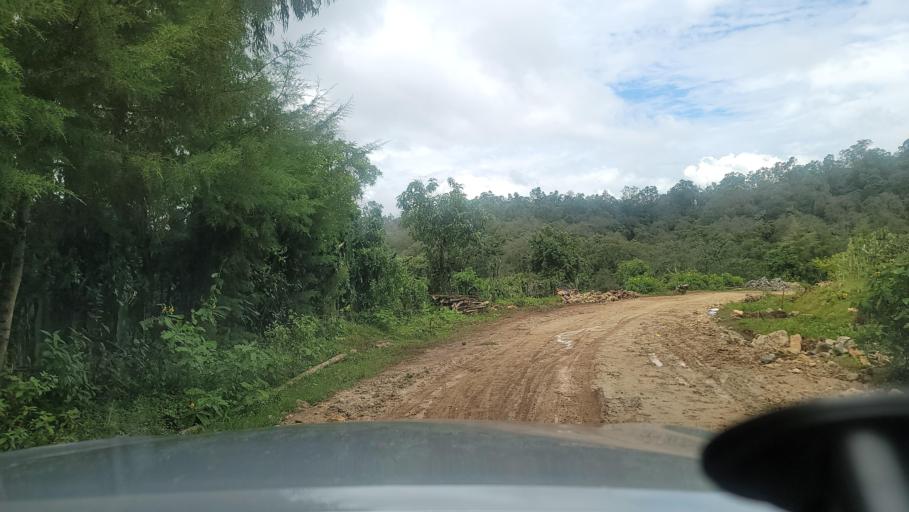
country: ET
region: Southern Nations, Nationalities, and People's Region
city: Bonga
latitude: 7.6319
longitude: 36.2216
